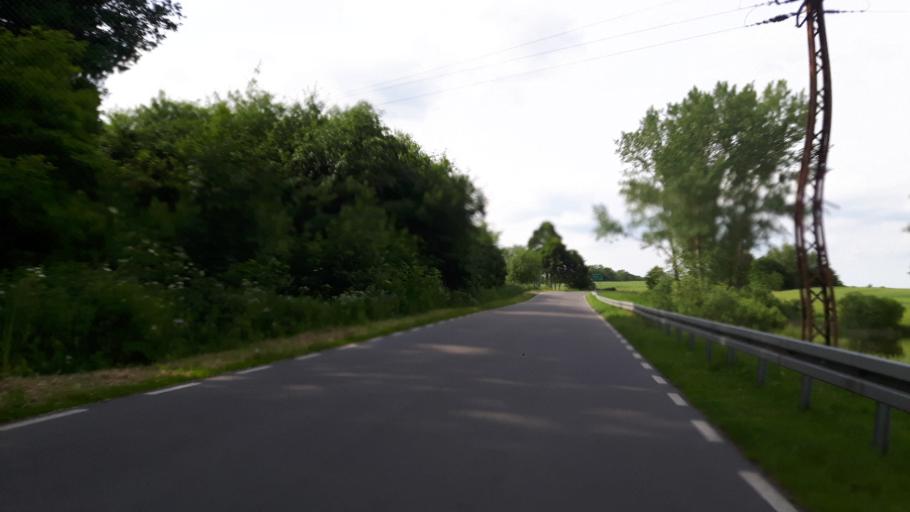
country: PL
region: West Pomeranian Voivodeship
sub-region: Powiat goleniowski
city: Nowogard
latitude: 53.7133
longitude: 15.1178
